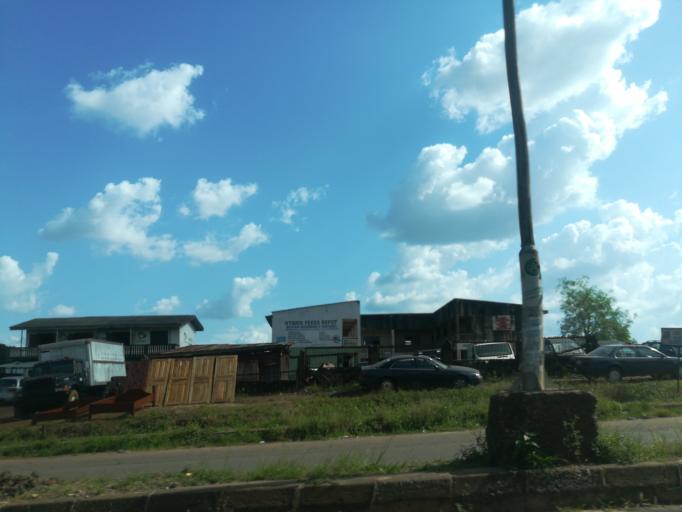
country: NG
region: Oyo
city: Egbeda
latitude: 7.4232
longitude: 3.9807
